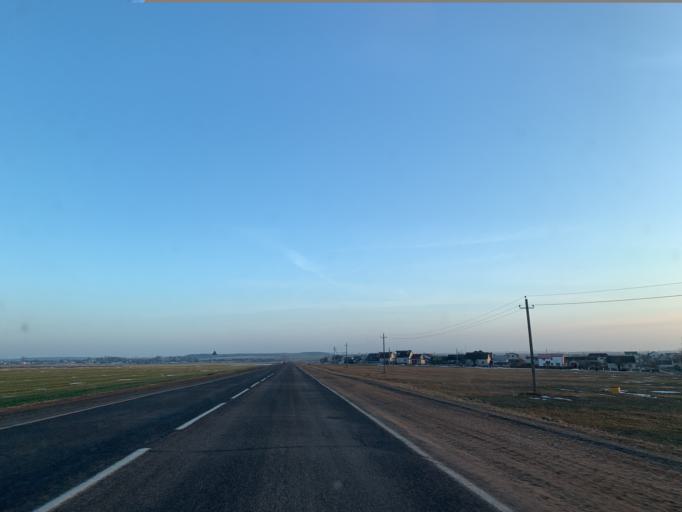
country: BY
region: Minsk
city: Haradzyeya
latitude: 53.3162
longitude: 26.5620
